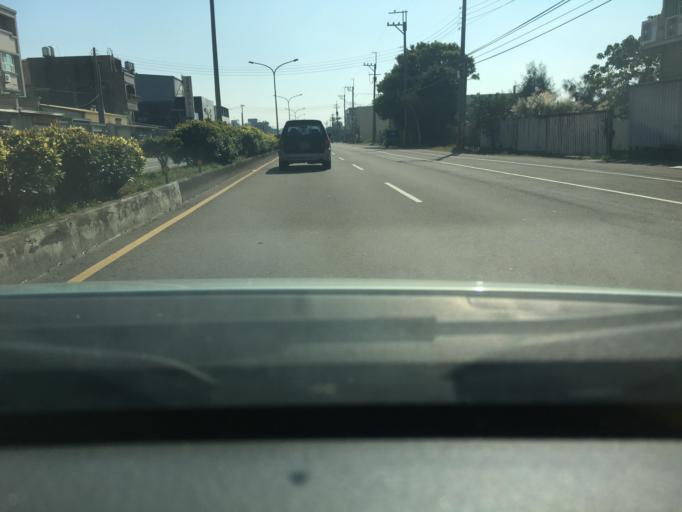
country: TW
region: Taiwan
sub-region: Hsinchu
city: Hsinchu
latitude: 24.8164
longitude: 120.9232
